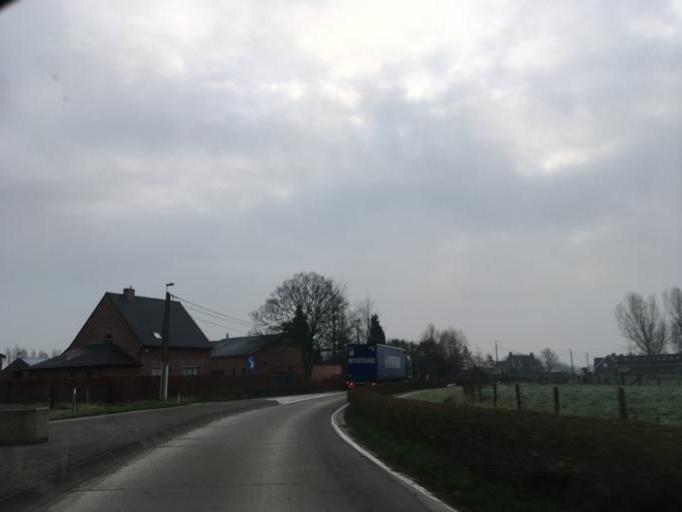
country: BE
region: Flanders
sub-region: Provincie West-Vlaanderen
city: Oostrozebeke
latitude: 50.9392
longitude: 3.3398
